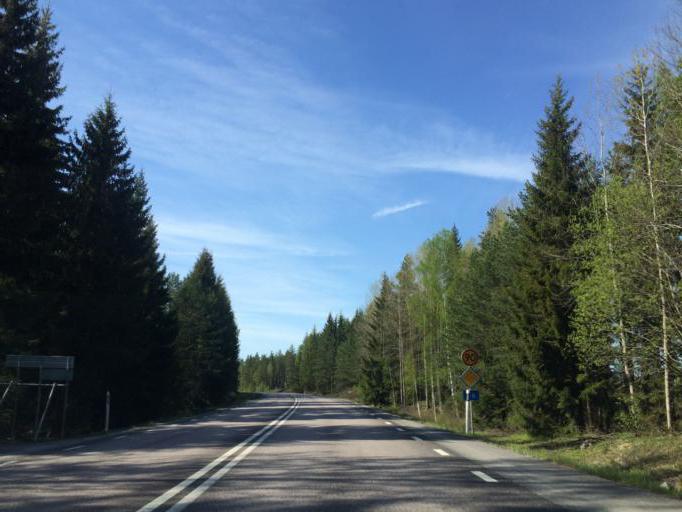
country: SE
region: Soedermanland
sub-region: Katrineholms Kommun
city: Katrineholm
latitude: 59.0717
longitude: 16.2223
